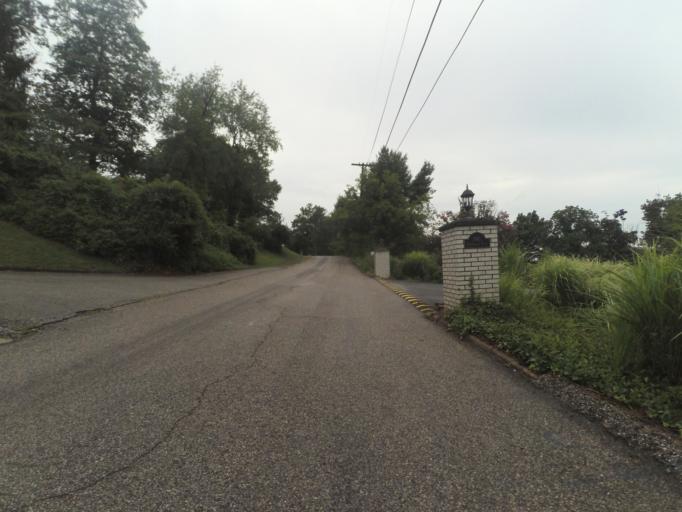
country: US
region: West Virginia
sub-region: Cabell County
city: Huntington
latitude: 38.4031
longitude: -82.4422
